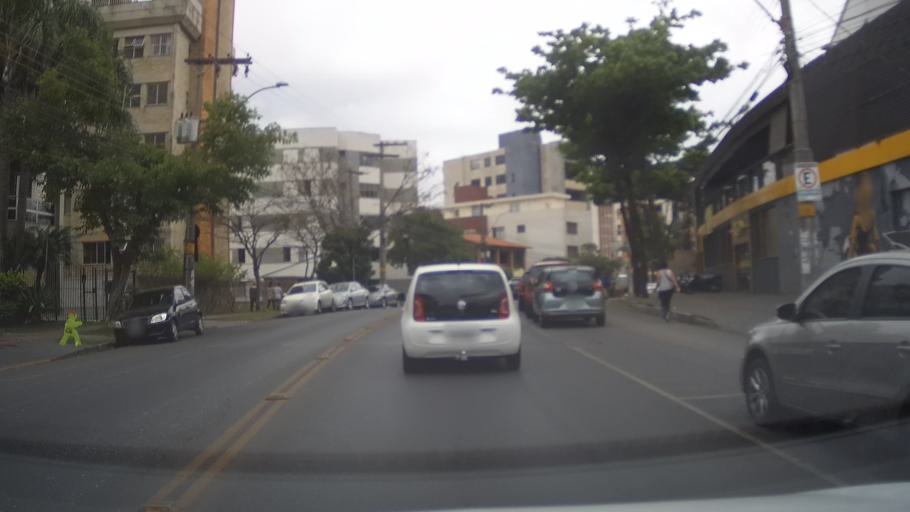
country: BR
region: Minas Gerais
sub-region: Belo Horizonte
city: Belo Horizonte
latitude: -19.9509
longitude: -43.9223
